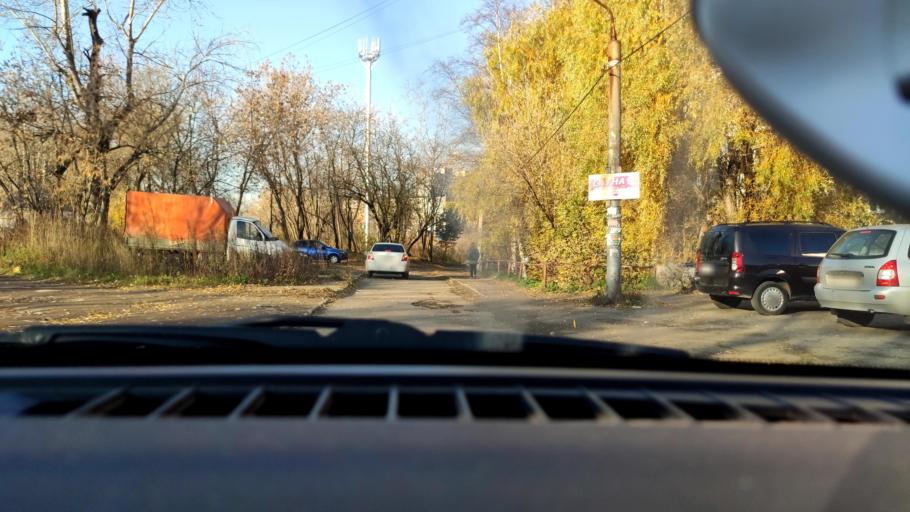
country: RU
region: Perm
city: Perm
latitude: 57.9615
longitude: 56.2325
